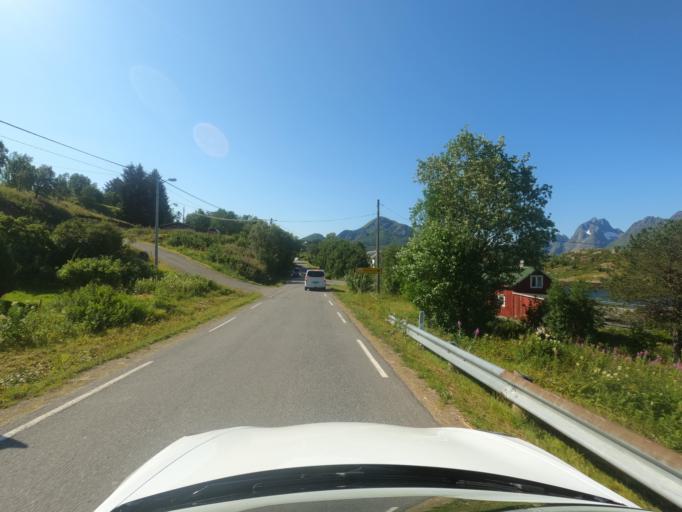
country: NO
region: Nordland
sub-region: Hadsel
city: Stokmarknes
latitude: 68.3152
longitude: 14.9904
